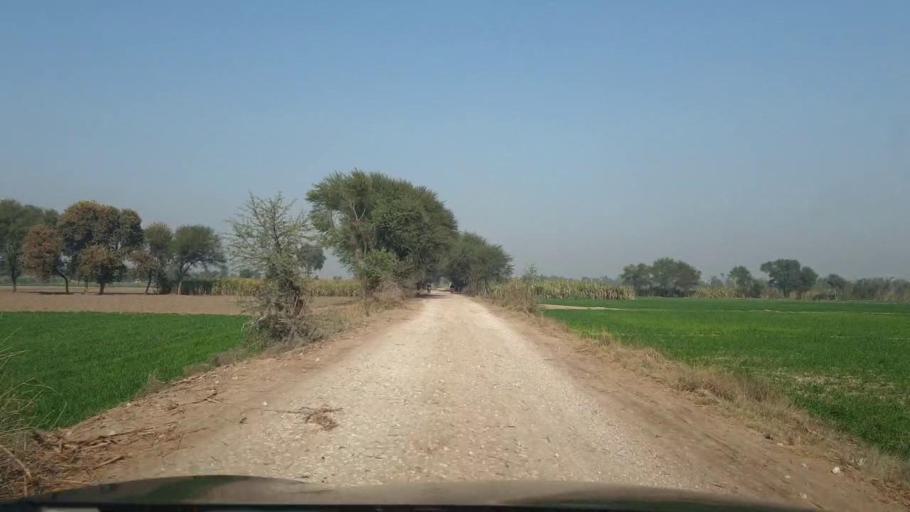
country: PK
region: Sindh
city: Ubauro
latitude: 28.1155
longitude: 69.7512
